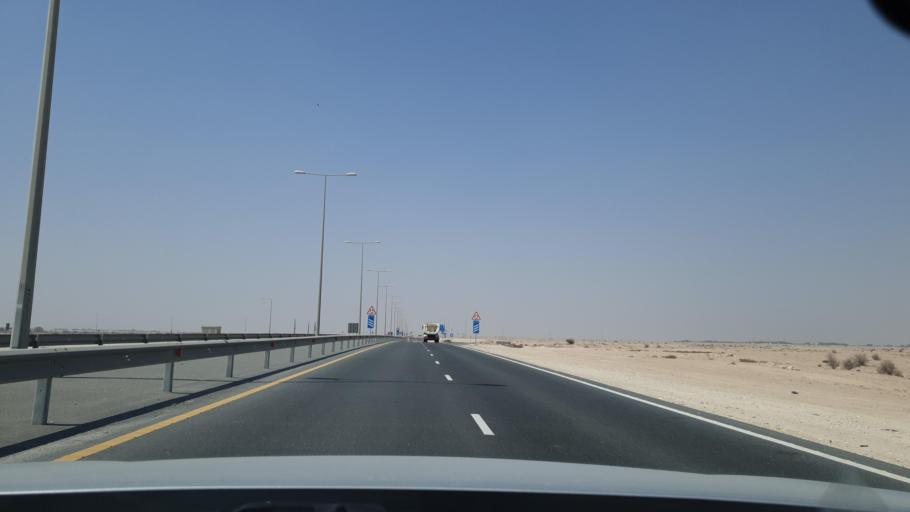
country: QA
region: Baladiyat az Za`ayin
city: Az Za`ayin
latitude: 25.6222
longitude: 51.3462
